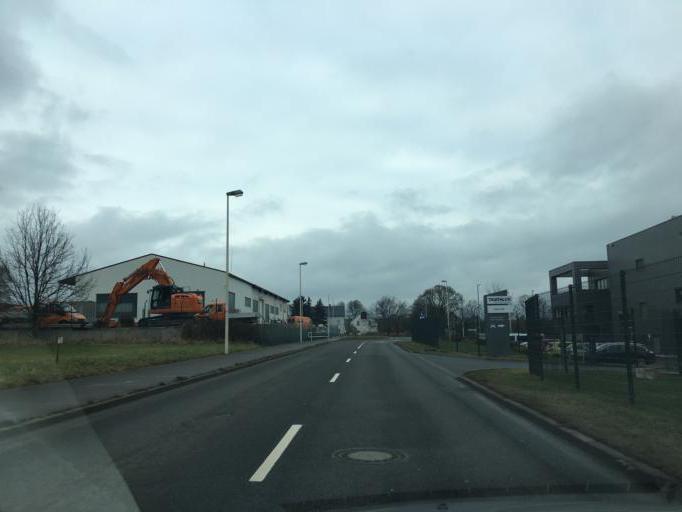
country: DE
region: Saxony
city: Pfaffroda
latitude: 50.8371
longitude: 12.5209
